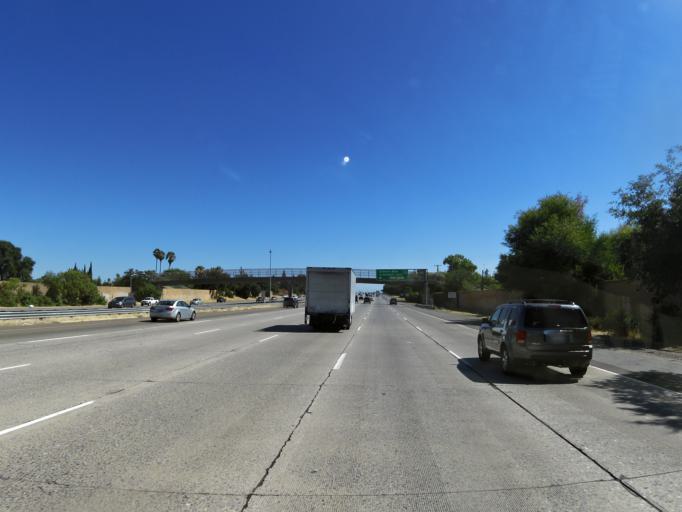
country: US
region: California
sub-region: Sacramento County
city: Foothill Farms
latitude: 38.6737
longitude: -121.3460
